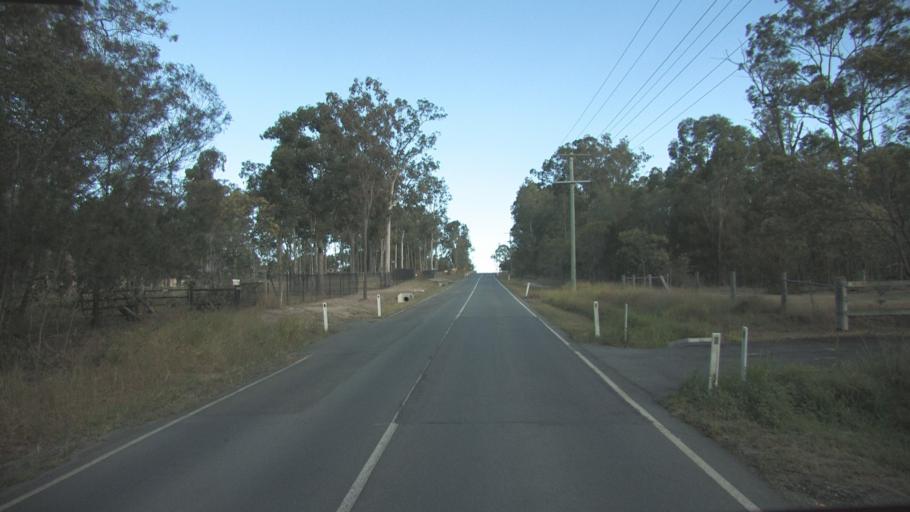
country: AU
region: Queensland
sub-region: Logan
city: Cedar Vale
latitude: -27.8282
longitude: 153.0534
